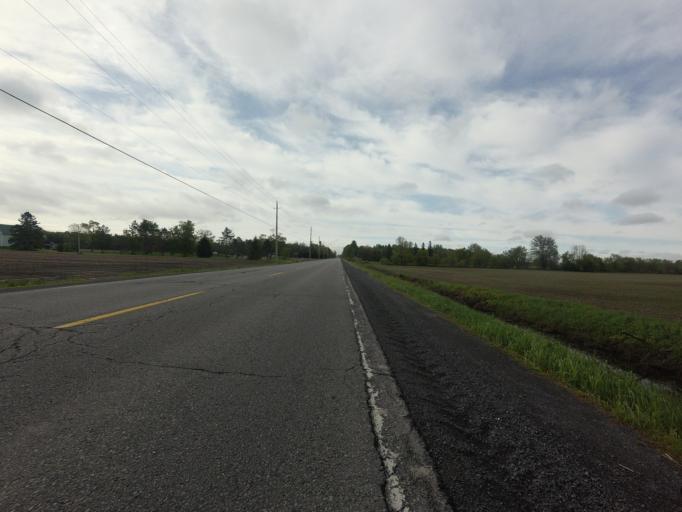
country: CA
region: Ontario
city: Bourget
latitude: 45.2429
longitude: -75.3499
